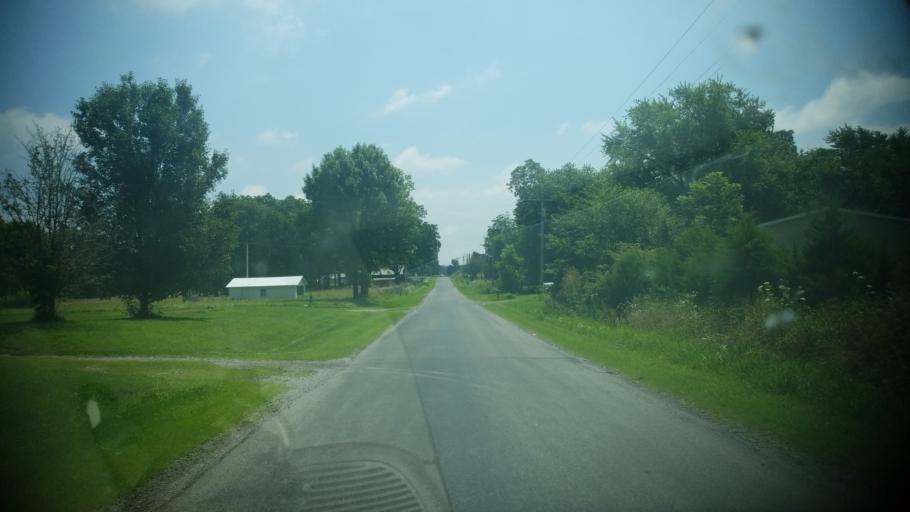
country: US
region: Illinois
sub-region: Wayne County
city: Fairfield
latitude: 38.5224
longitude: -88.3574
